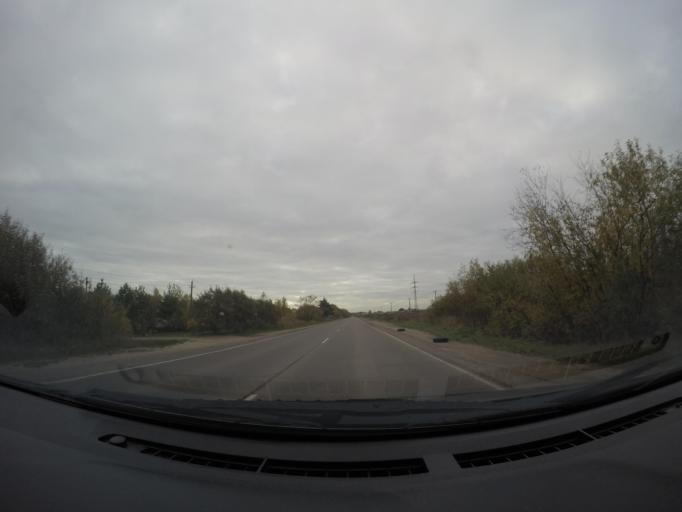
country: RU
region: Moskovskaya
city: Staraya Kupavna
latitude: 55.7723
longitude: 38.1976
